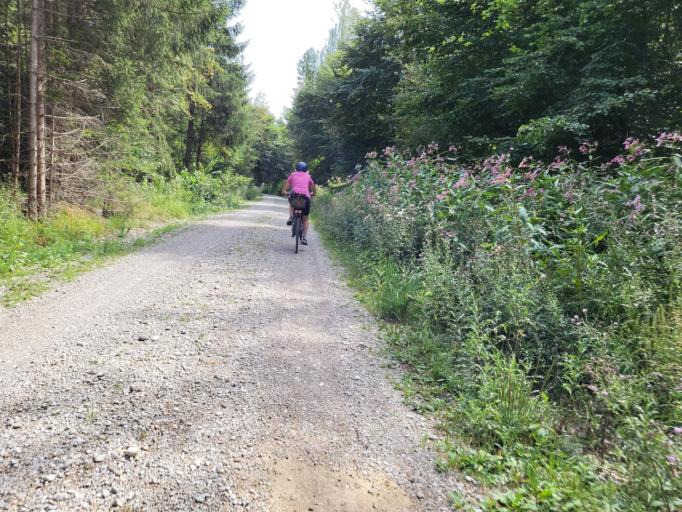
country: DE
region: Bavaria
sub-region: Upper Bavaria
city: Hohenkirchen-Siegertsbrunn
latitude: 48.0387
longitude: 11.7469
